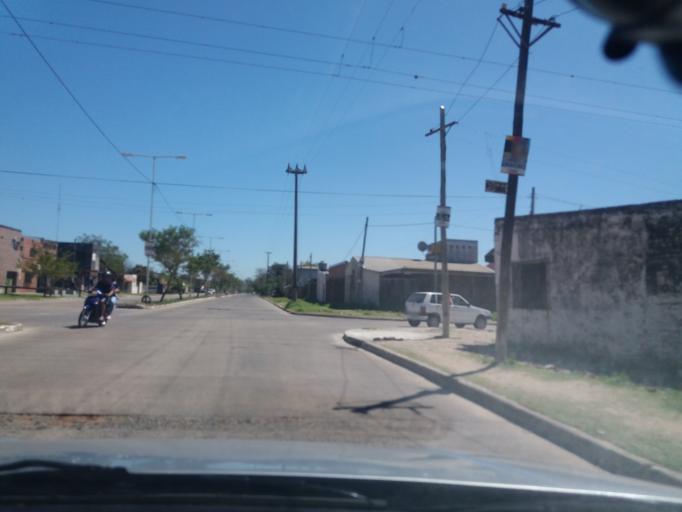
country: AR
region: Corrientes
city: Corrientes
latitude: -27.4888
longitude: -58.8401
